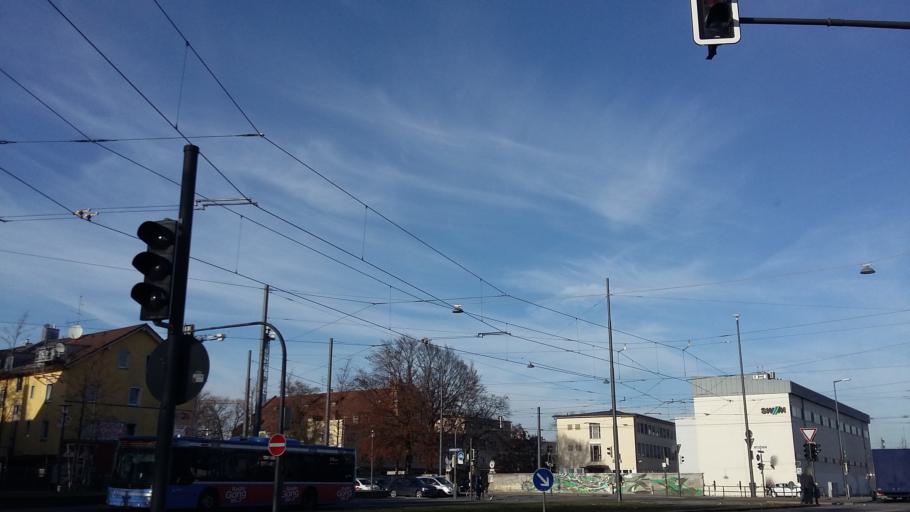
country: DE
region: Bavaria
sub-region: Upper Bavaria
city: Pasing
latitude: 48.1449
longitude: 11.4719
